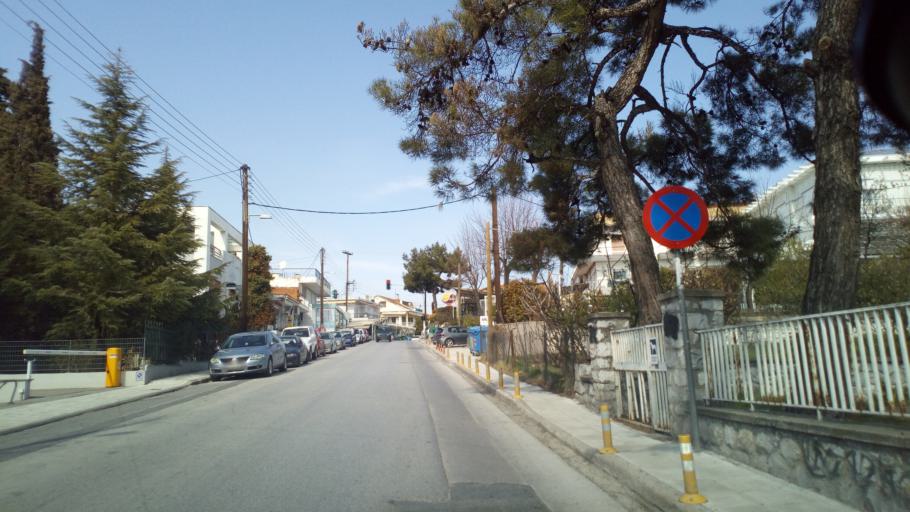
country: GR
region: Central Macedonia
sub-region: Nomos Thessalonikis
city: Panorama
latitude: 40.5903
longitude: 23.0368
